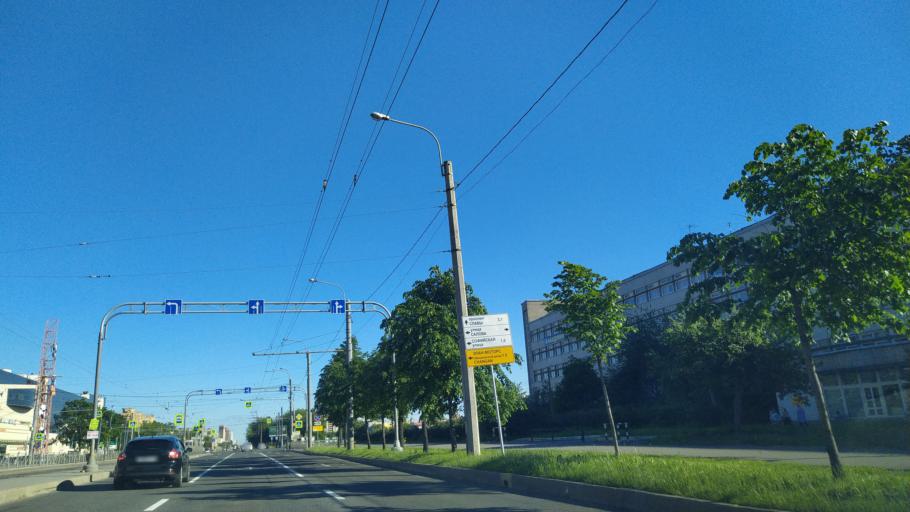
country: RU
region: St.-Petersburg
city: Kupchino
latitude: 59.8851
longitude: 30.3657
